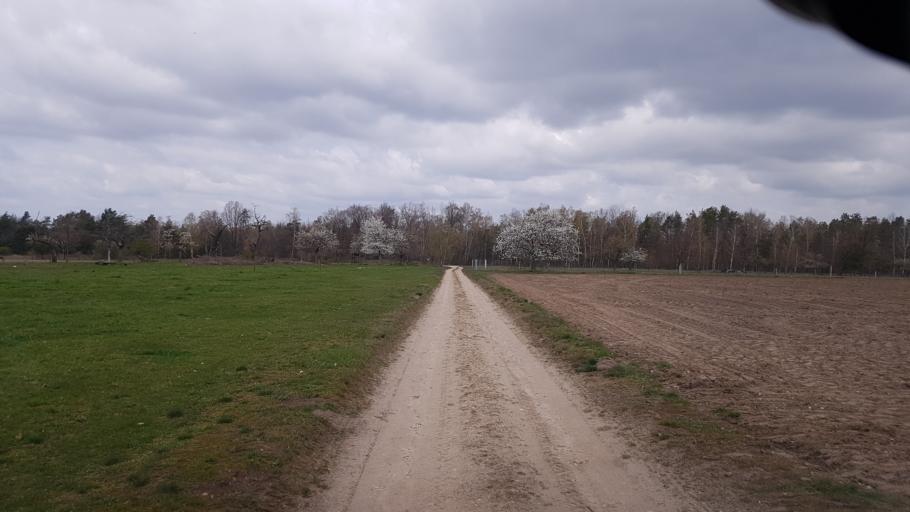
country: DE
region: Brandenburg
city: Hohenleipisch
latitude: 51.5049
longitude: 13.5479
